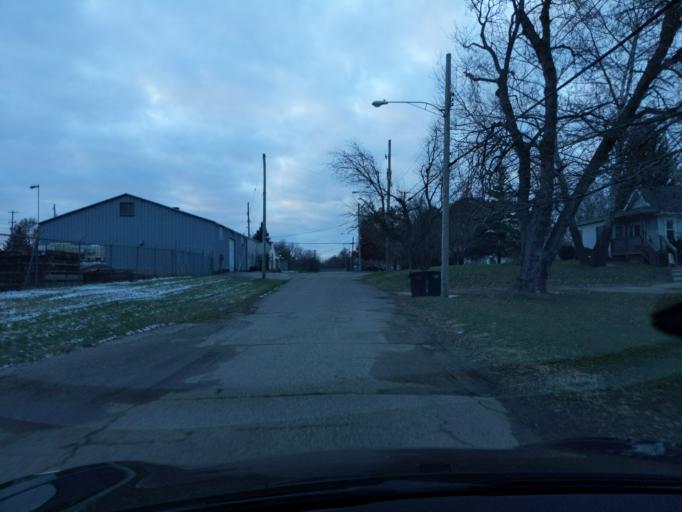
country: US
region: Michigan
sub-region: Ingham County
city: Lansing
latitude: 42.7646
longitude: -84.5395
